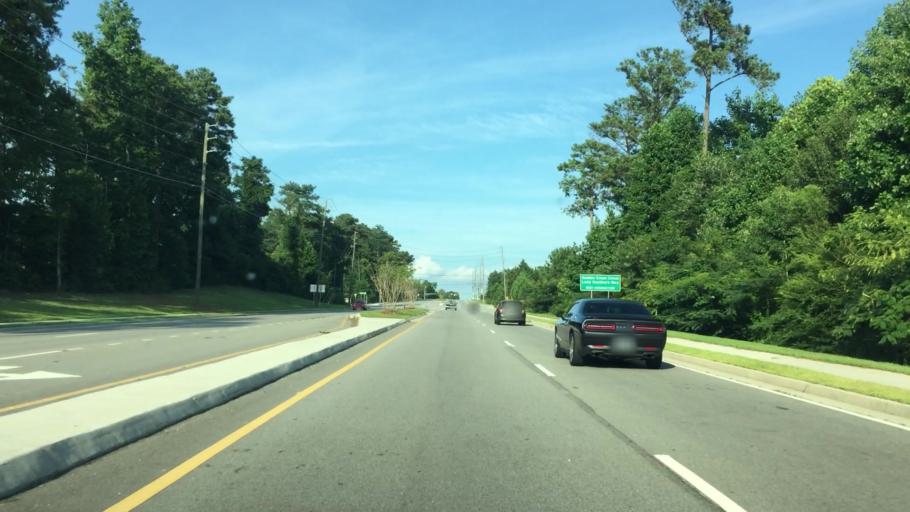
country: US
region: Georgia
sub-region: Clayton County
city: Lake City
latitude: 33.6104
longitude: -84.2766
